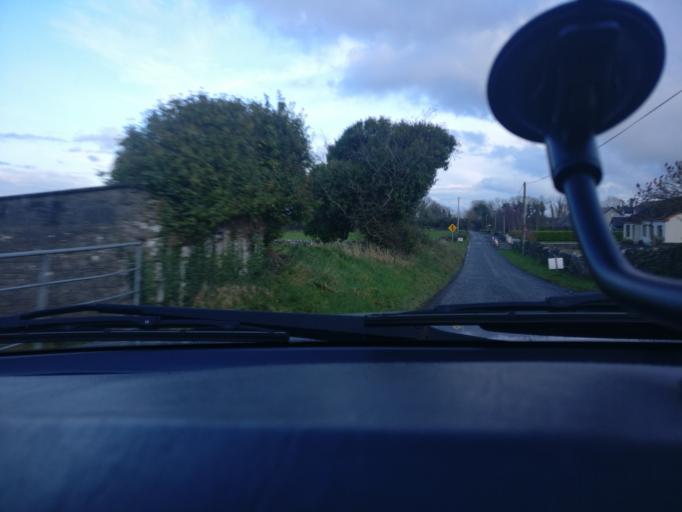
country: IE
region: Connaught
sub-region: County Galway
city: Loughrea
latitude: 53.1995
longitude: -8.6677
